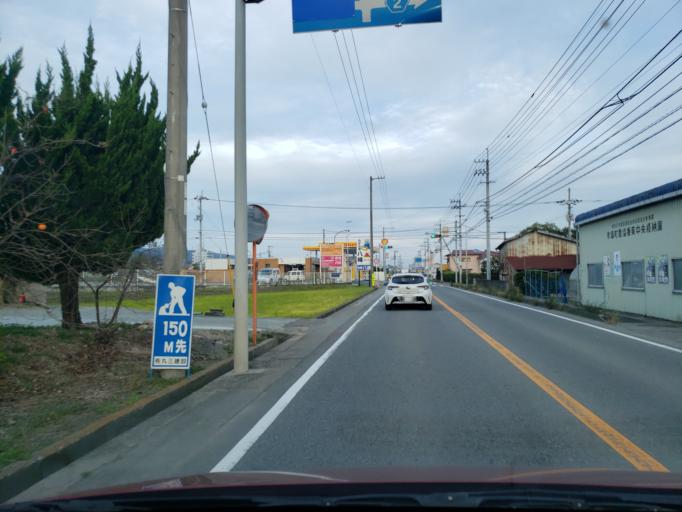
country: JP
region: Tokushima
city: Kamojimacho-jogejima
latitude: 34.0866
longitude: 134.2908
